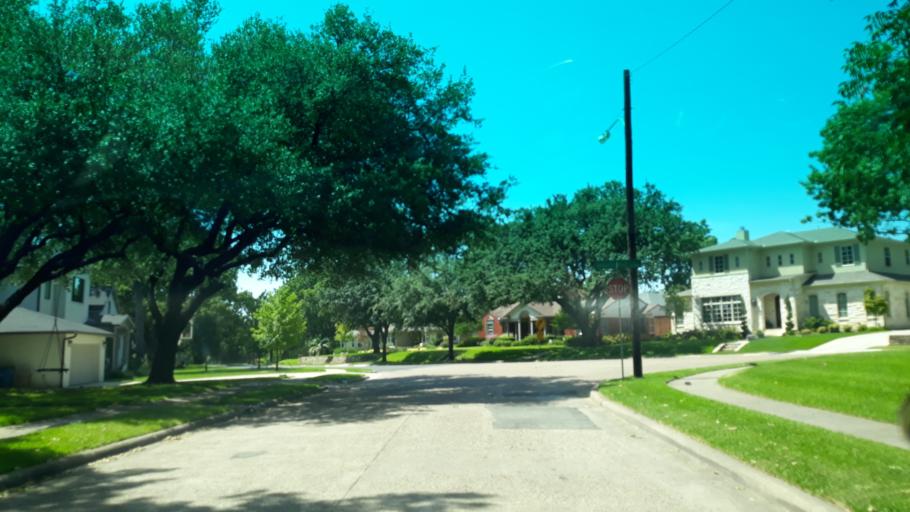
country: US
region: Texas
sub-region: Dallas County
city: Highland Park
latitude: 32.8289
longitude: -96.7445
